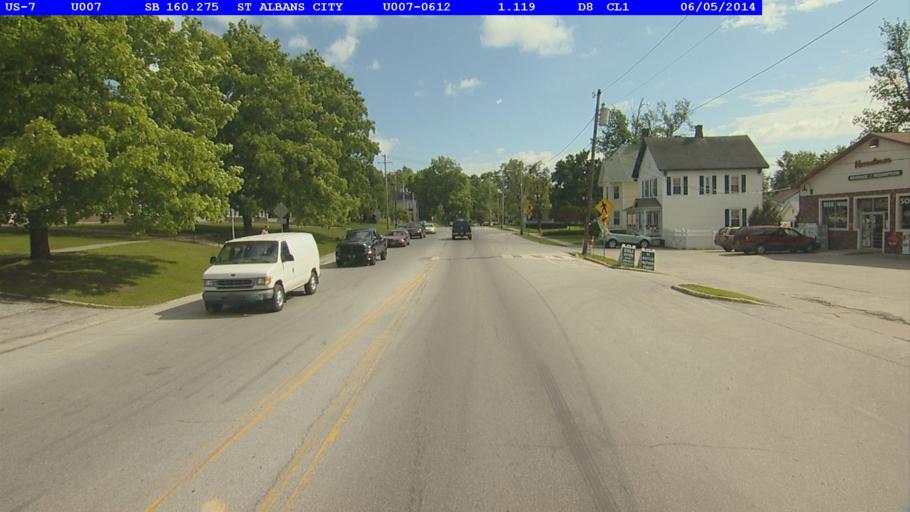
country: US
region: Vermont
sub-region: Franklin County
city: Saint Albans
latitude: 44.8089
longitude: -73.0839
